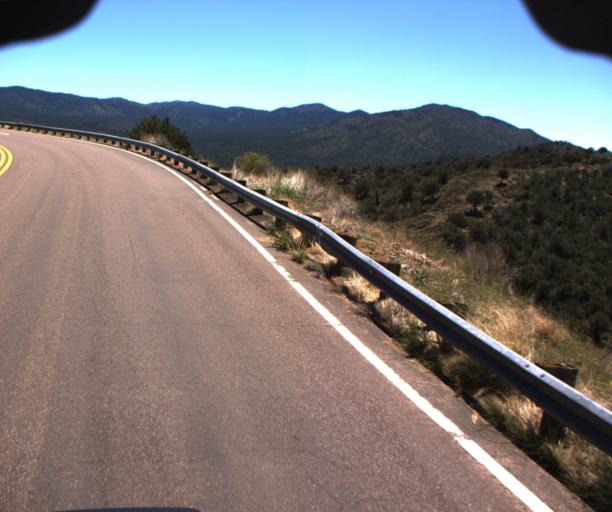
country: US
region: Arizona
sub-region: Yavapai County
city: Prescott
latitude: 34.4736
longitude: -112.5120
